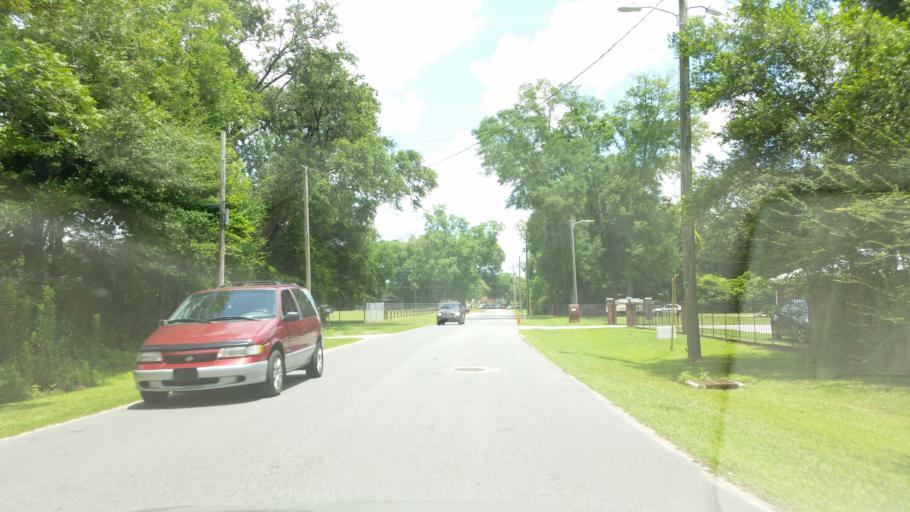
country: US
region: Florida
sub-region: Escambia County
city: Ensley
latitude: 30.5168
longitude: -87.2676
